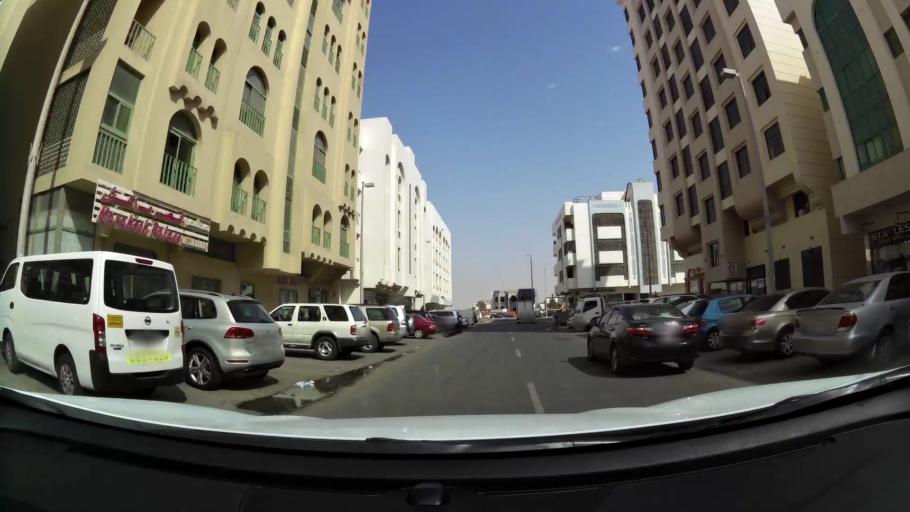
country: AE
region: Abu Dhabi
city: Abu Dhabi
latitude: 24.3376
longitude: 54.5375
